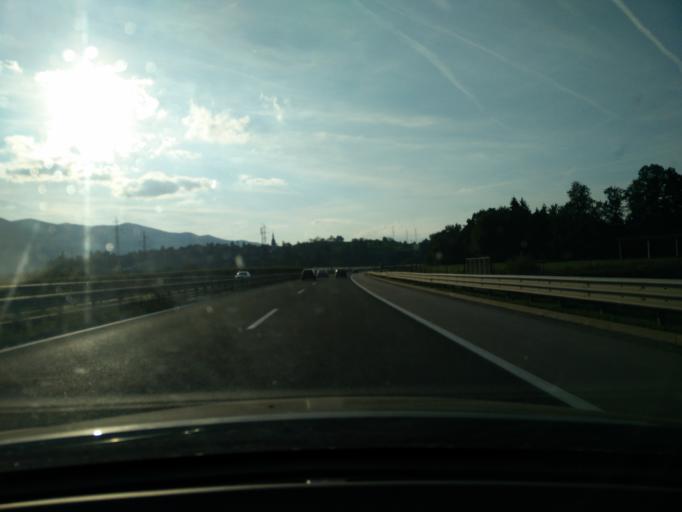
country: SI
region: Trzic
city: Bistrica pri Trzicu
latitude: 46.3141
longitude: 14.2572
